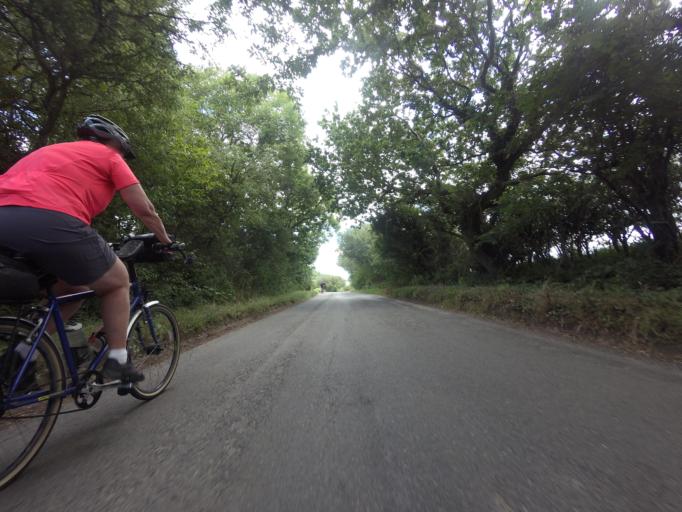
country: GB
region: England
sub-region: East Sussex
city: Hailsham
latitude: 50.8397
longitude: 0.1846
